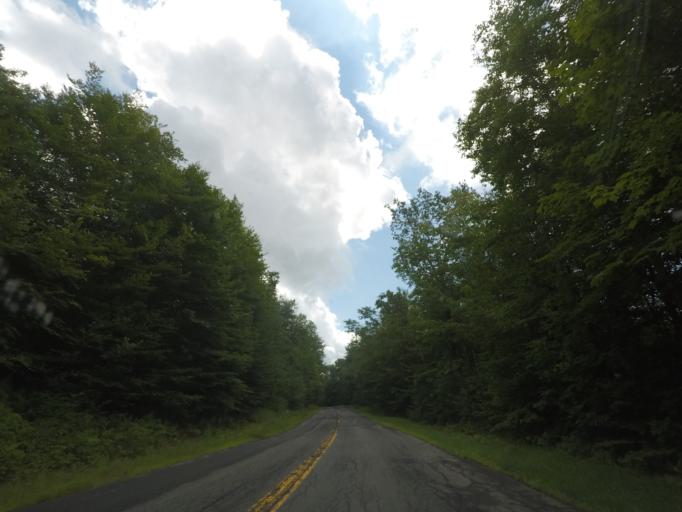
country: US
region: New York
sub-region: Rensselaer County
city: Averill Park
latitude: 42.6714
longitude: -73.4208
